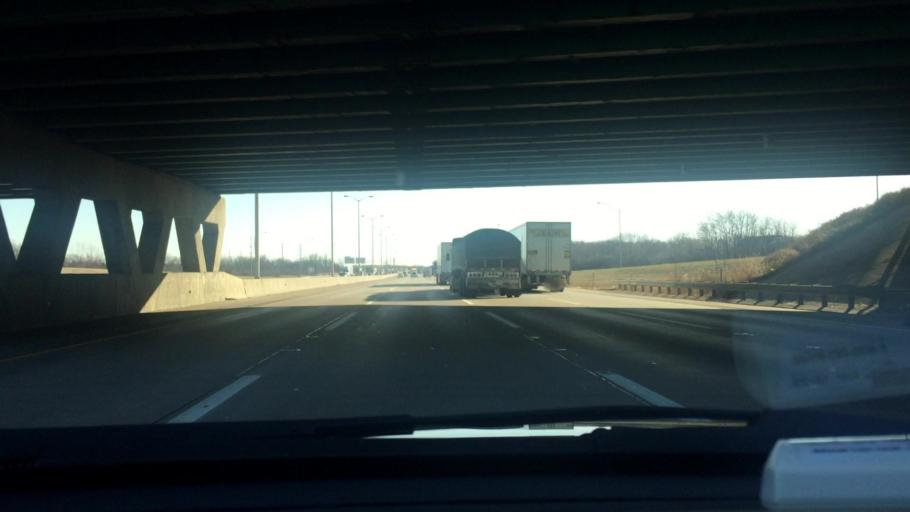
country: US
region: Illinois
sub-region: Lake County
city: Green Oaks
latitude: 42.3117
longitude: -87.9050
